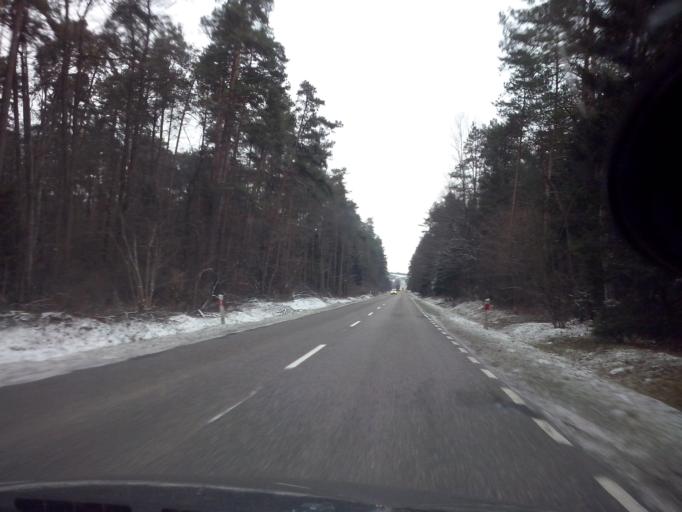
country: PL
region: Lublin Voivodeship
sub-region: Powiat bilgorajski
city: Tereszpol
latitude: 50.5953
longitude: 22.8635
